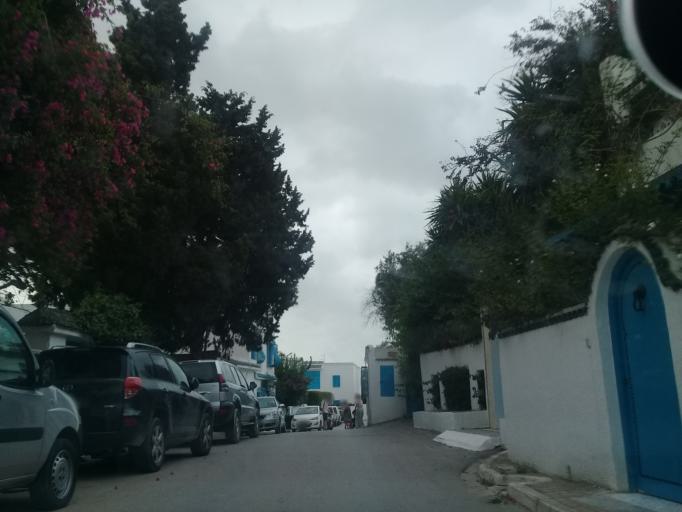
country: TN
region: Tunis
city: Sidi Bou Said
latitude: 36.8728
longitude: 10.3418
